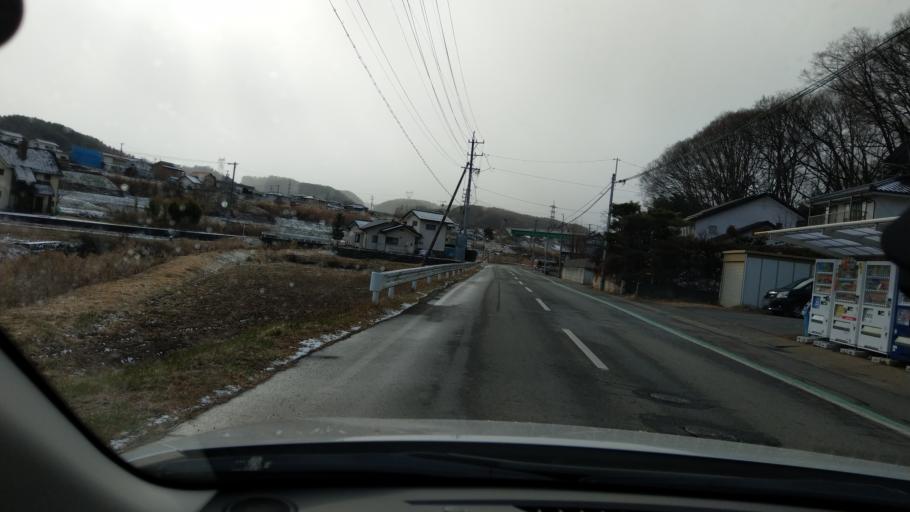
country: JP
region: Nagano
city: Saku
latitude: 36.1657
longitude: 138.4769
